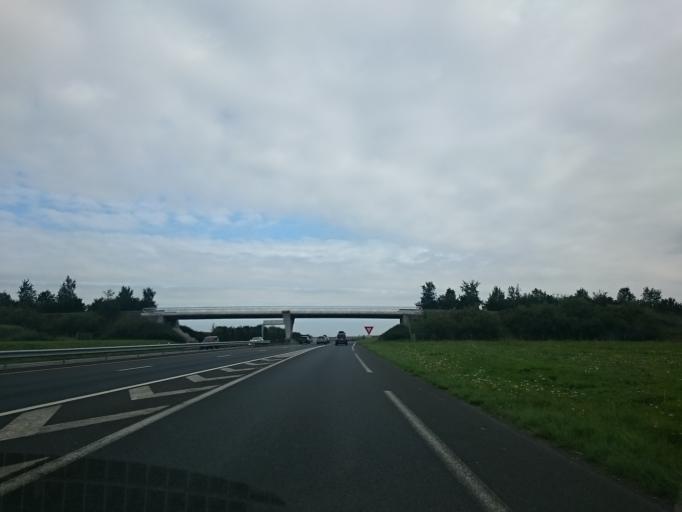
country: FR
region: Lower Normandy
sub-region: Departement de la Manche
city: Ducey
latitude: 48.5873
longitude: -1.3283
